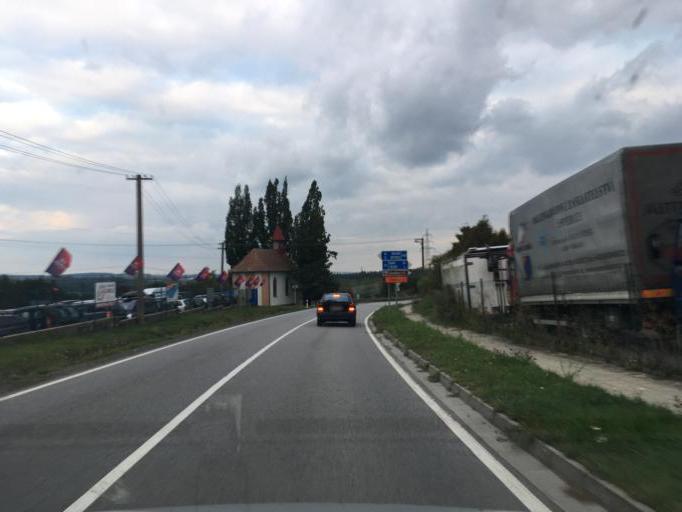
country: CZ
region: Vysocina
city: Starec
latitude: 49.2133
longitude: 15.8281
